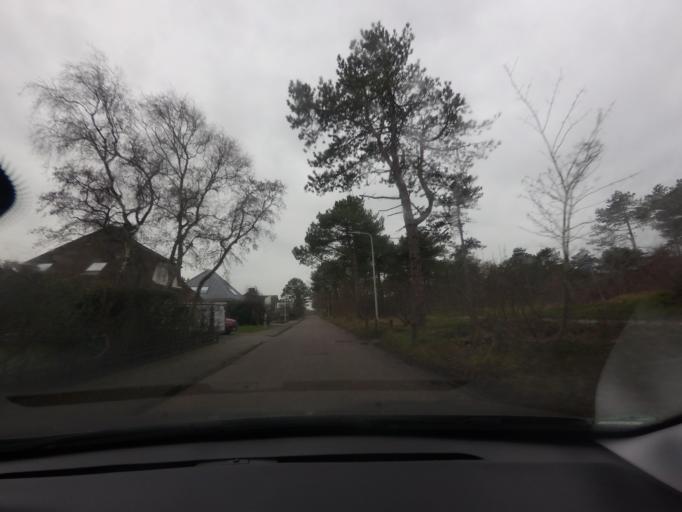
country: NL
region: North Holland
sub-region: Gemeente Texel
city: Den Burg
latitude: 53.0947
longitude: 4.7582
